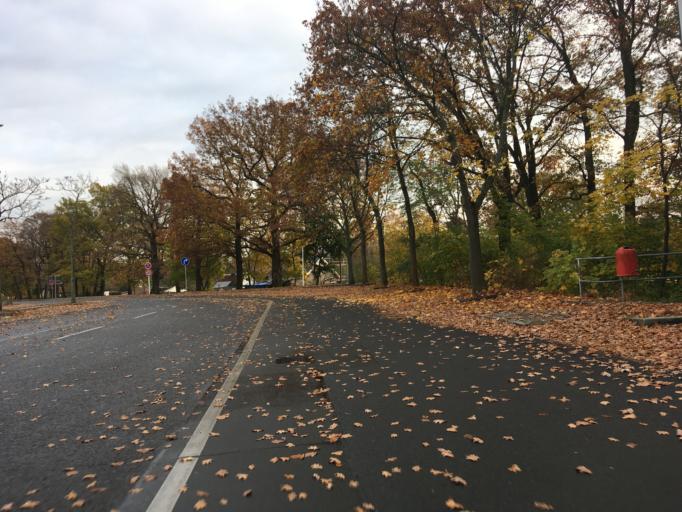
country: DE
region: Berlin
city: Charlottenburg-Nord
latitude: 52.5515
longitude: 13.2855
